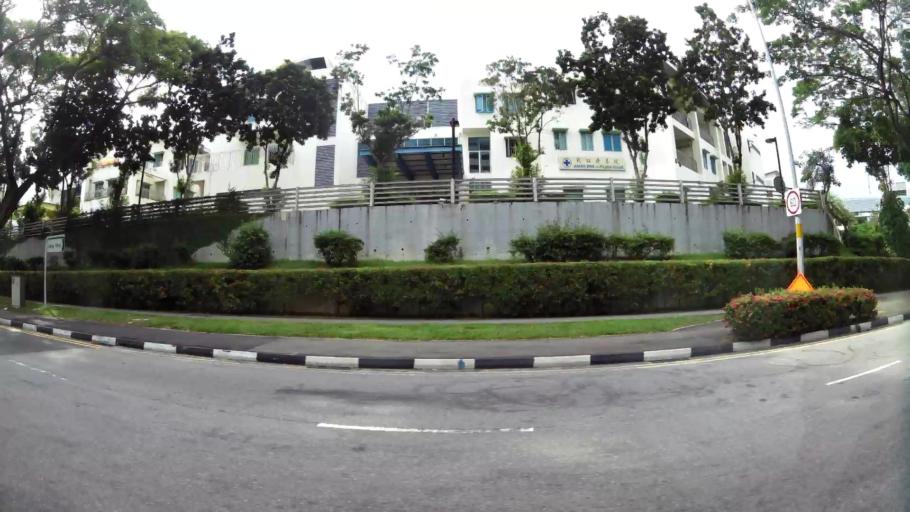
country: MY
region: Johor
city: Kampung Pasir Gudang Baru
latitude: 1.3810
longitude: 103.8876
